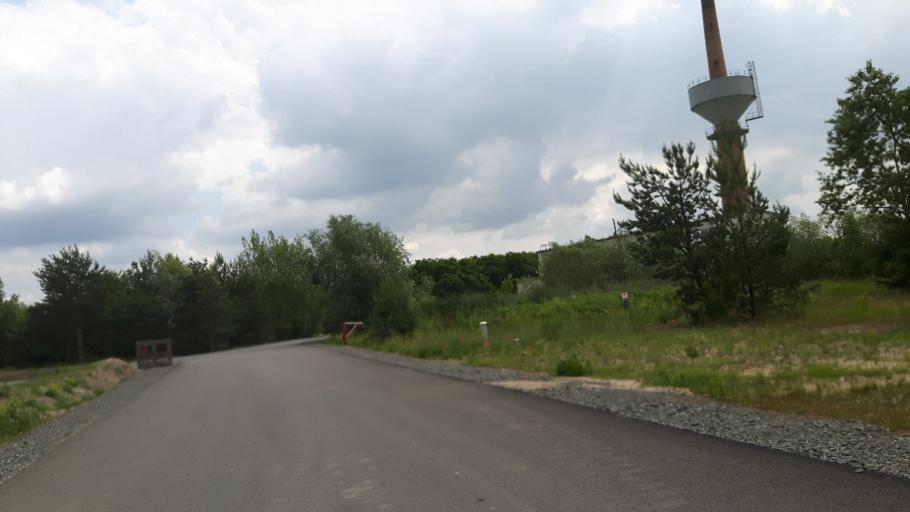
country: DE
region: Saxony-Anhalt
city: Grafenhainichen
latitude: 51.6951
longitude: 12.4559
